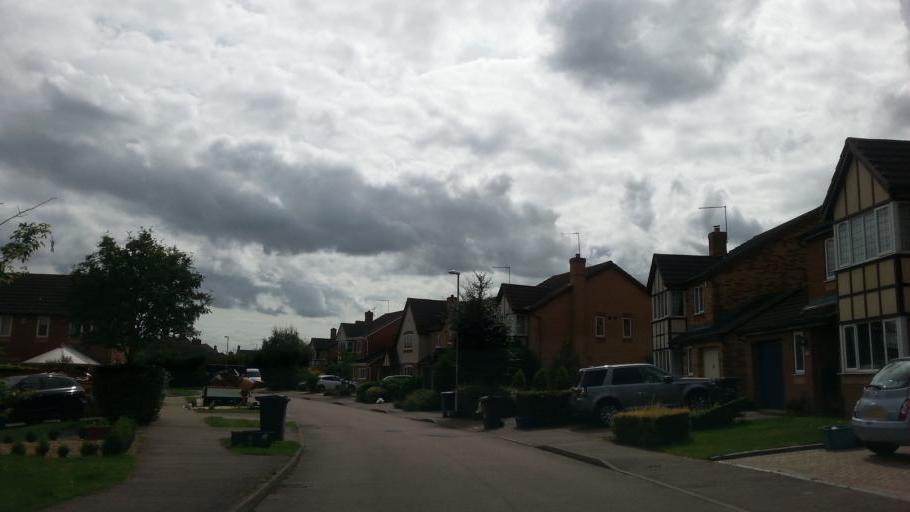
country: GB
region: England
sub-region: Northamptonshire
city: Hardingstone
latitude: 52.2340
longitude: -0.9394
